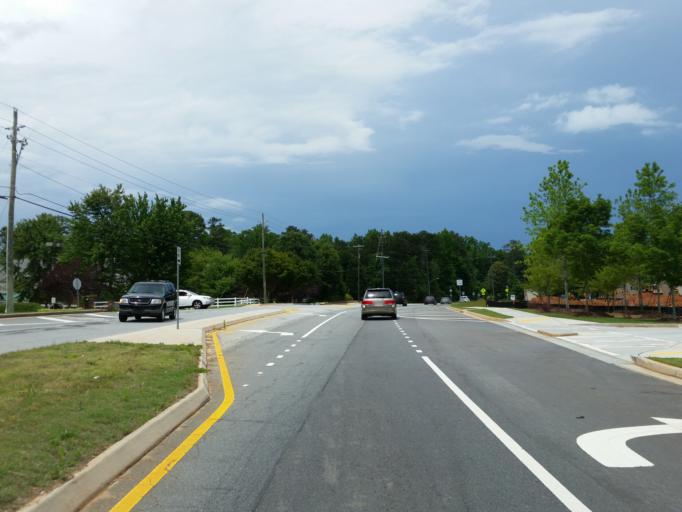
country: US
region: Georgia
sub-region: Fulton County
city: Roswell
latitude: 34.0634
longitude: -84.3952
